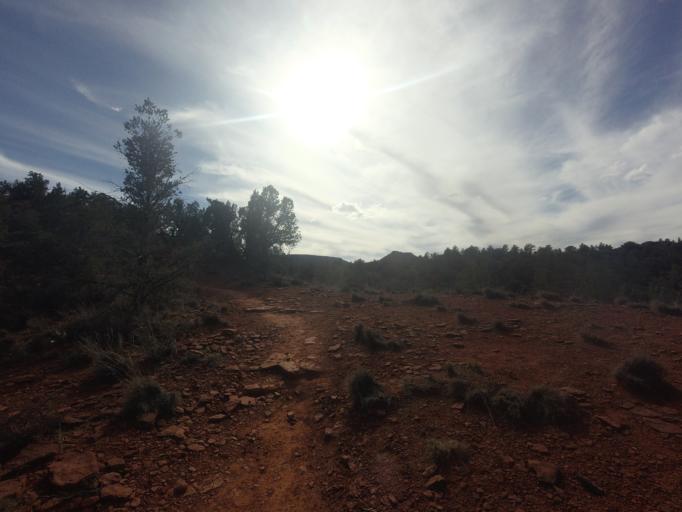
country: US
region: Arizona
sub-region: Yavapai County
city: West Sedona
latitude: 34.8075
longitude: -111.8301
